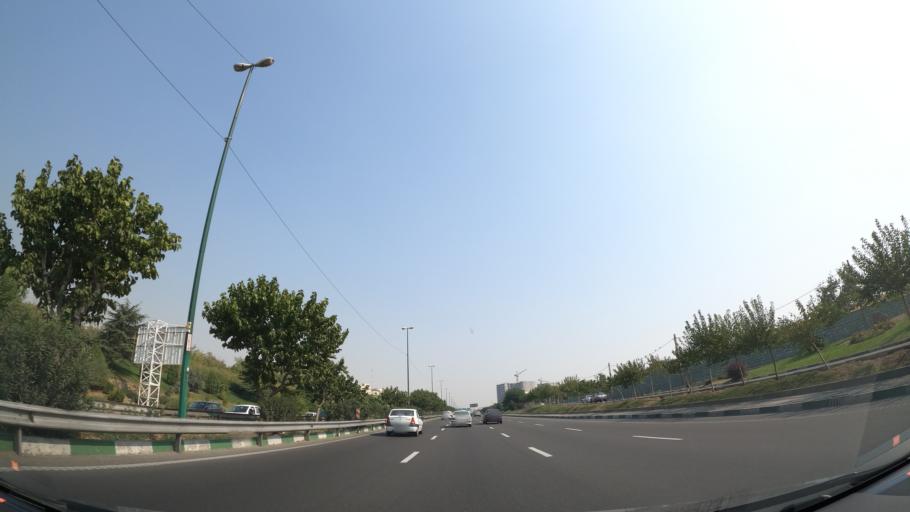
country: IR
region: Tehran
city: Tehran
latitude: 35.7537
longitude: 51.2796
